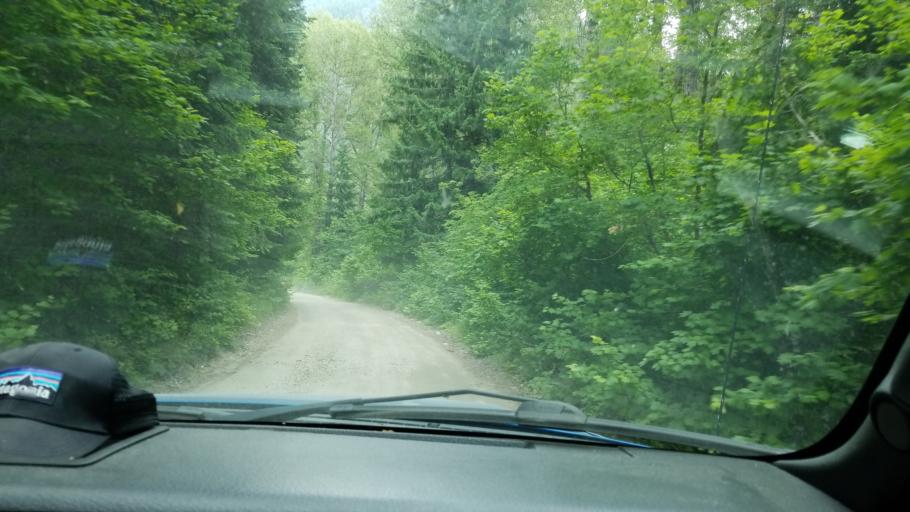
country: US
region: Washington
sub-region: Chelan County
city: Leavenworth
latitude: 47.9232
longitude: -120.9005
